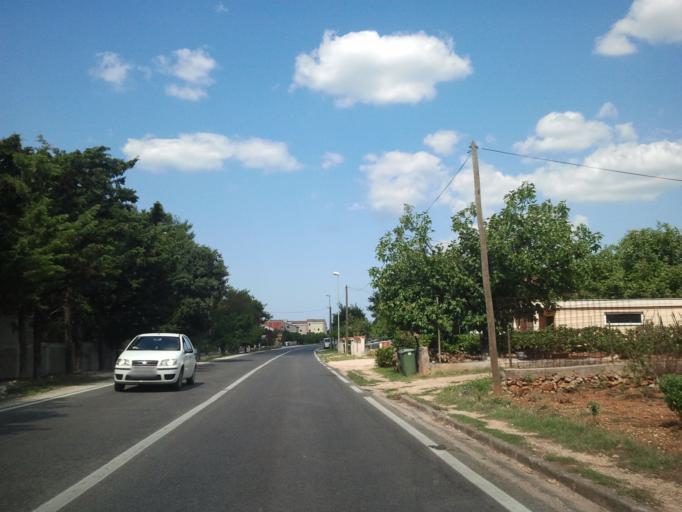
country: HR
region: Zadarska
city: Turanj
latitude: 43.9720
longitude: 15.4040
